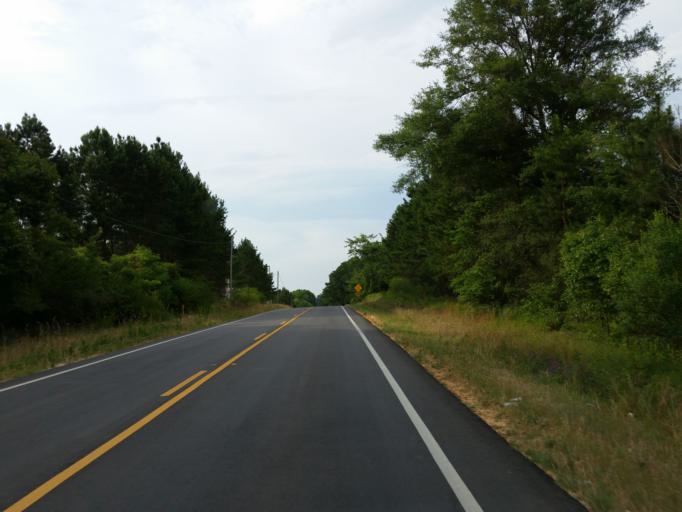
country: US
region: Georgia
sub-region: Turner County
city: Ashburn
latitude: 31.7361
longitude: -83.6665
